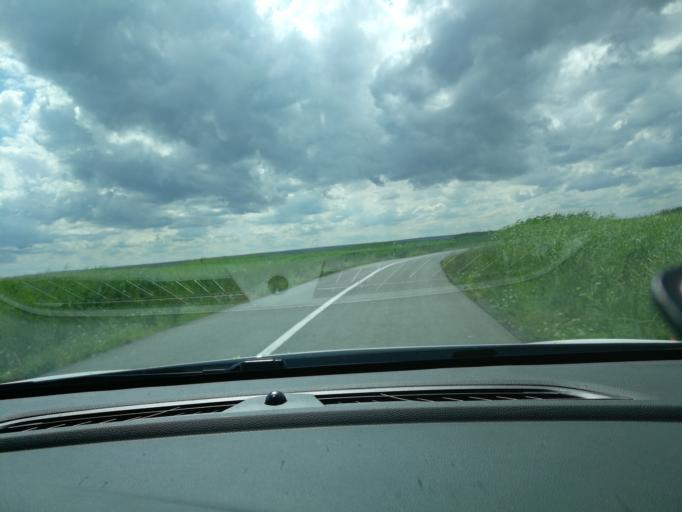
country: RO
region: Constanta
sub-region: Comuna Istria
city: Istria
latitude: 44.5347
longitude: 28.7296
